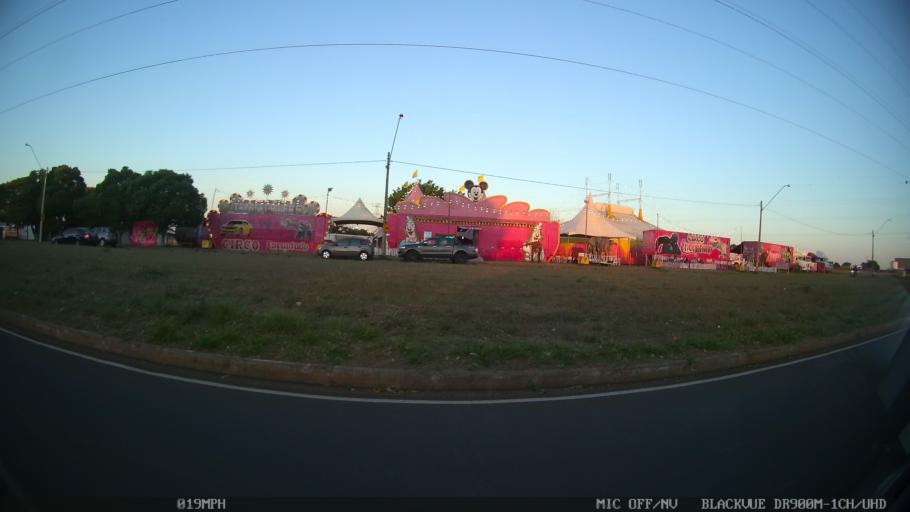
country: BR
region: Sao Paulo
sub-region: Sao Jose Do Rio Preto
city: Sao Jose do Rio Preto
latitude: -20.7949
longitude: -49.3450
